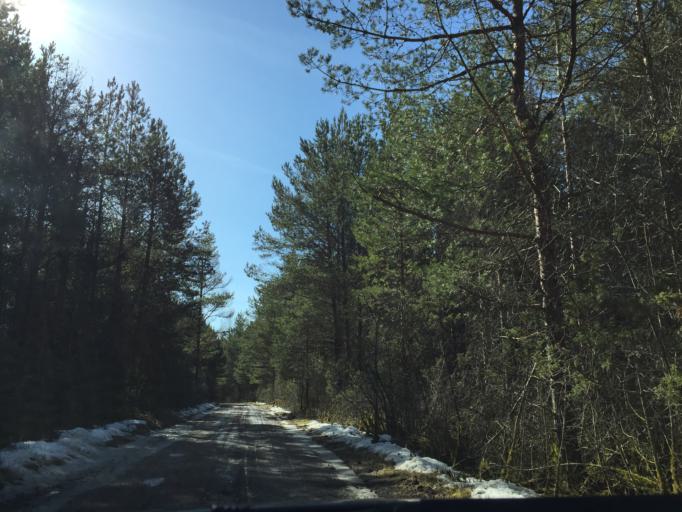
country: EE
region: Laeaene
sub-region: Haapsalu linn
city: Haapsalu
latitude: 58.6402
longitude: 23.5176
